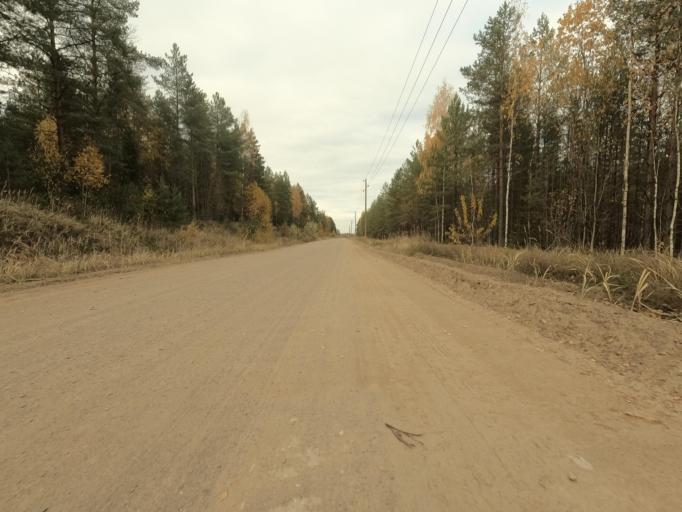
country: RU
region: Leningrad
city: Priladozhskiy
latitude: 59.6959
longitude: 31.3617
